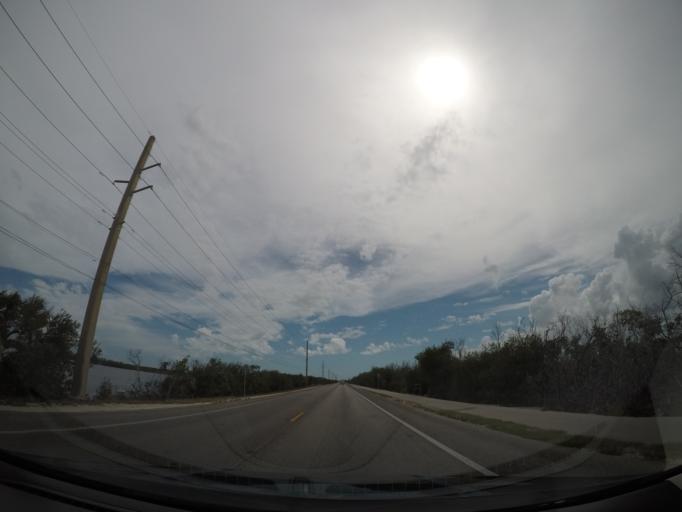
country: US
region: Florida
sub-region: Monroe County
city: Big Pine Key
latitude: 24.6662
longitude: -81.2597
